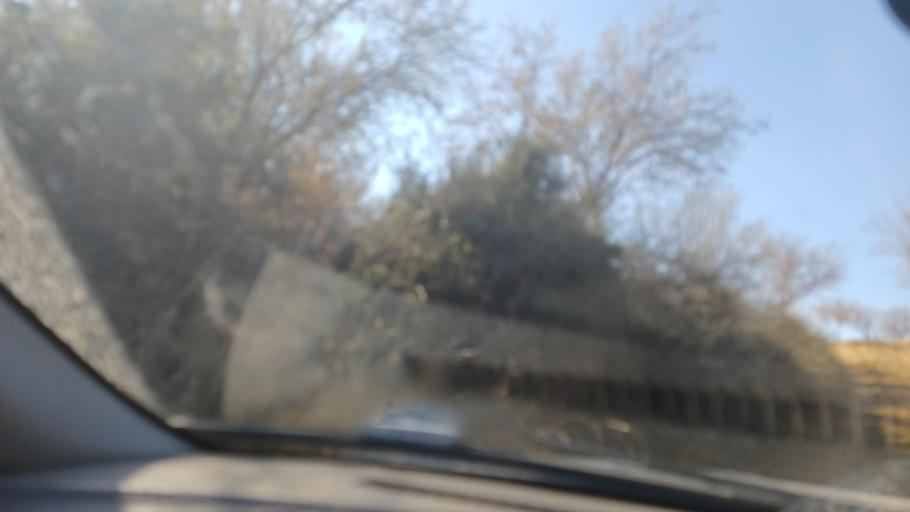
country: CY
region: Pafos
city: Polis
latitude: 34.9478
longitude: 32.4822
